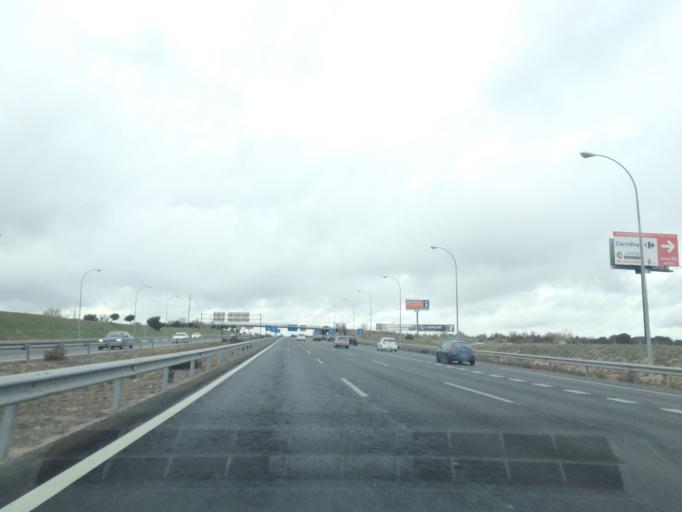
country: ES
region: Madrid
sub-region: Provincia de Madrid
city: Pozuelo de Alarcon
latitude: 40.4190
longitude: -3.8272
